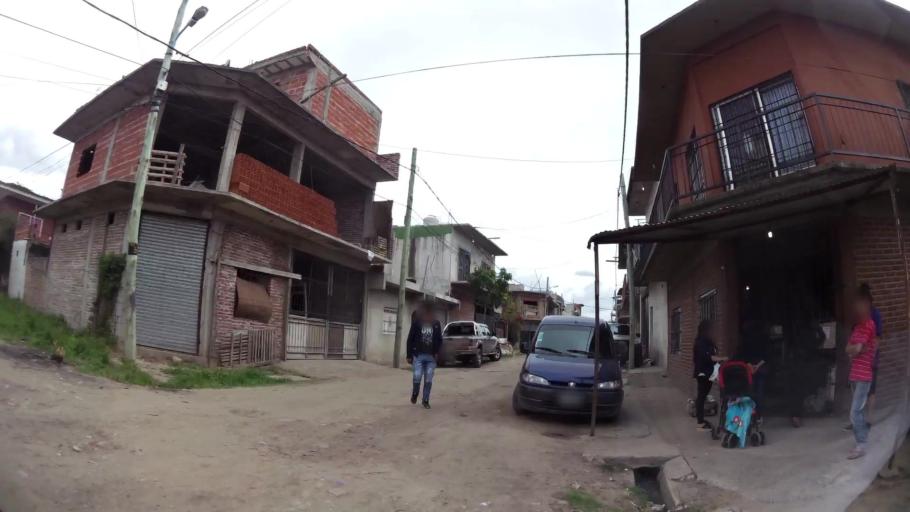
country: AR
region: Buenos Aires
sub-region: Partido de Quilmes
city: Quilmes
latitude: -34.7564
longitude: -58.2560
